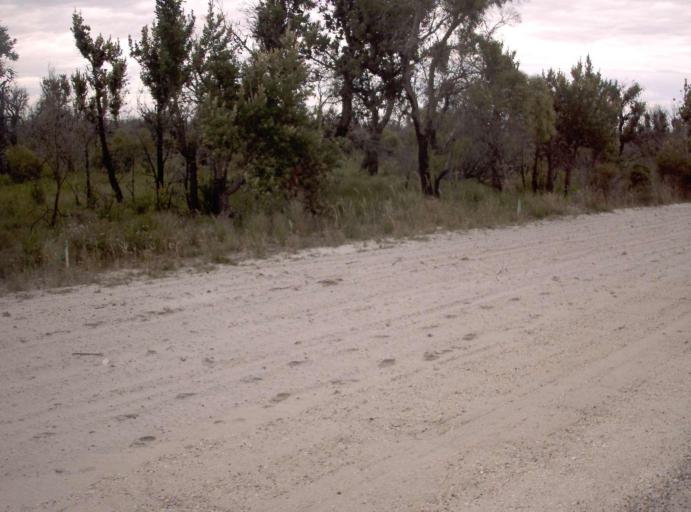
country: AU
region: Victoria
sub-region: East Gippsland
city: Bairnsdale
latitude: -38.1237
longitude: 147.4511
